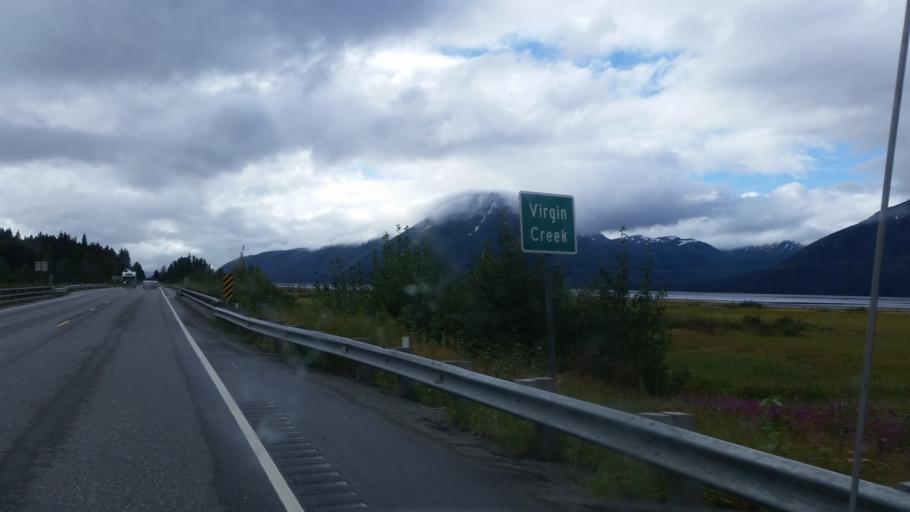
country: US
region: Alaska
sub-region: Anchorage Municipality
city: Girdwood
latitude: 60.9335
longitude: -149.1559
